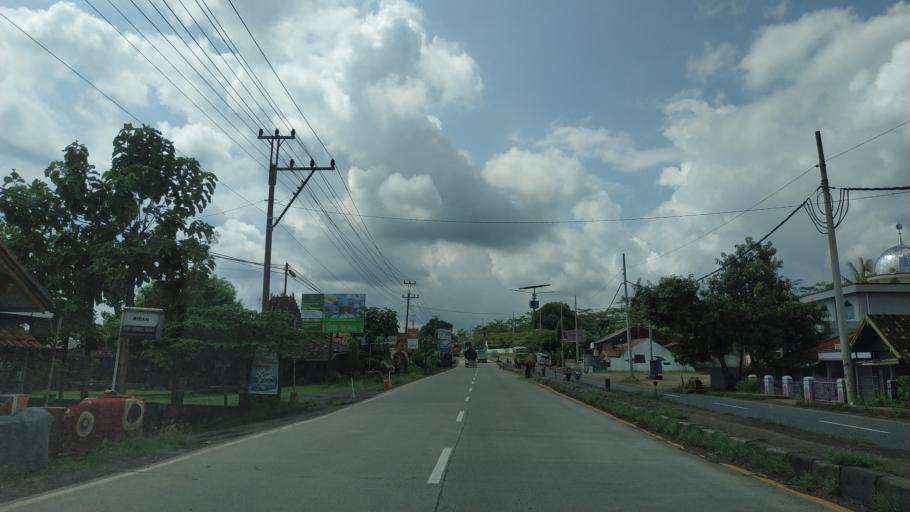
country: ID
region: Central Java
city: Pekalongan
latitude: -6.9448
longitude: 109.8102
